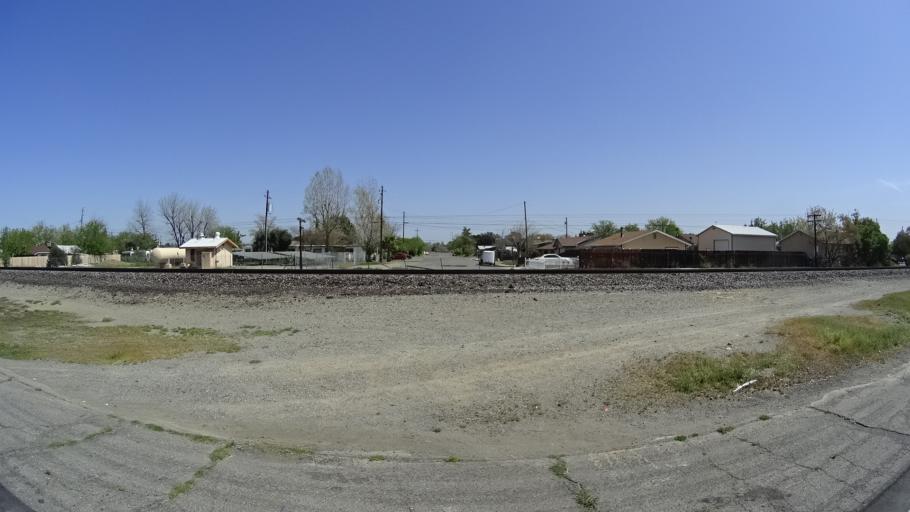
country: US
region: California
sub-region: Glenn County
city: Orland
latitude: 39.7532
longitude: -122.1970
